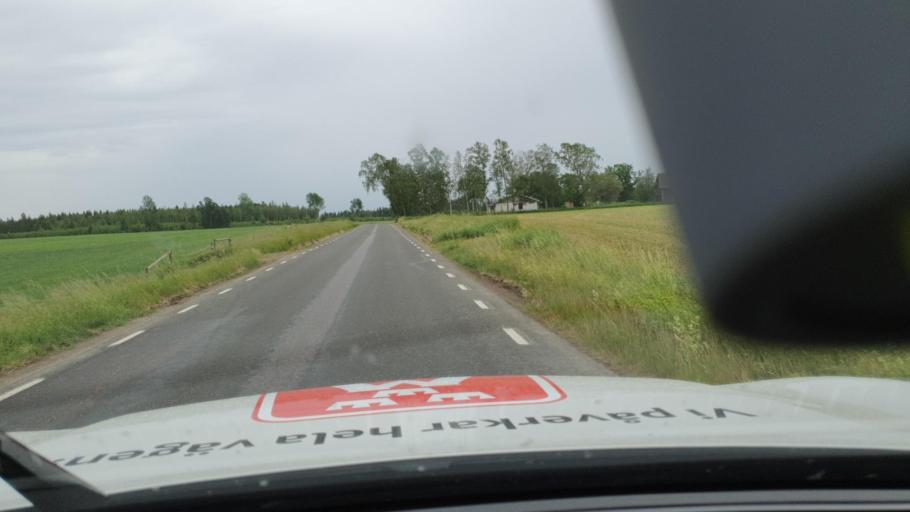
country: SE
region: Vaestra Goetaland
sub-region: Tidaholms Kommun
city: Olofstorp
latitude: 58.3269
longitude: 14.0600
